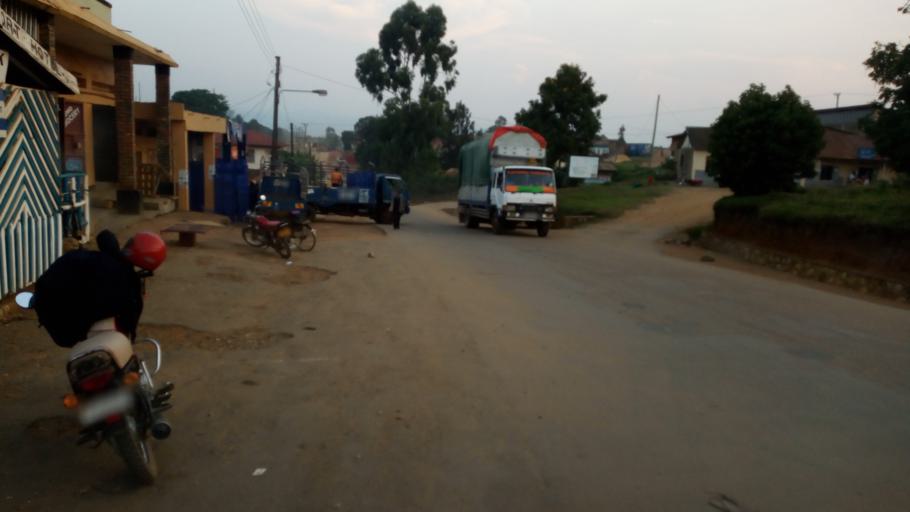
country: UG
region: Western Region
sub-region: Rukungiri District
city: Rukungiri
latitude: -0.7932
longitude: 29.9252
